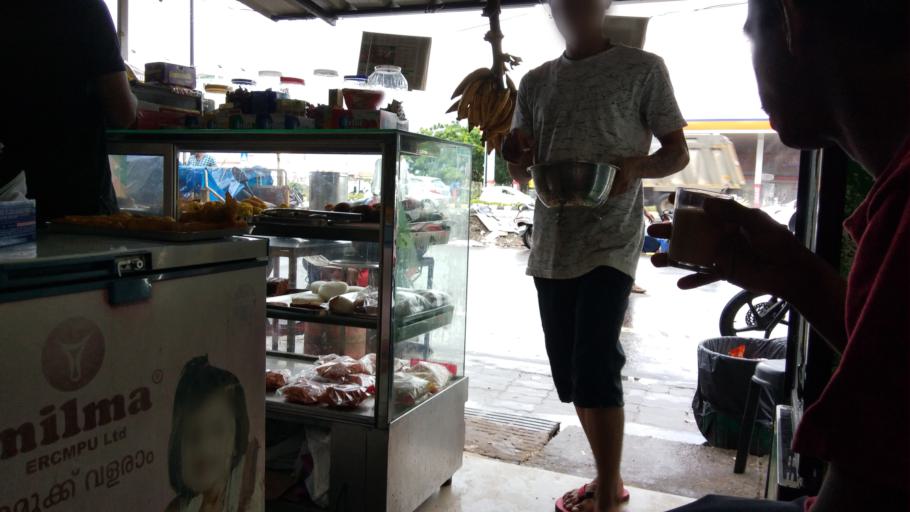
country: IN
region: Kerala
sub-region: Ernakulam
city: Angamali
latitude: 10.1596
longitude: 76.3860
